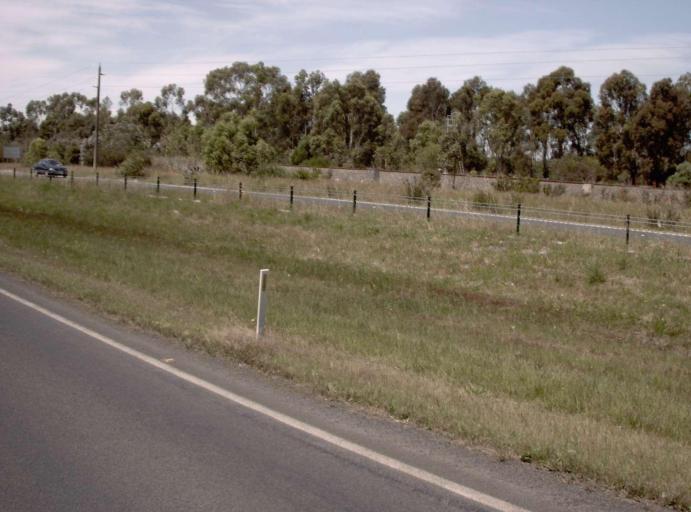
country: AU
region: Victoria
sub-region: Latrobe
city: Morwell
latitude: -38.2230
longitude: 146.4682
